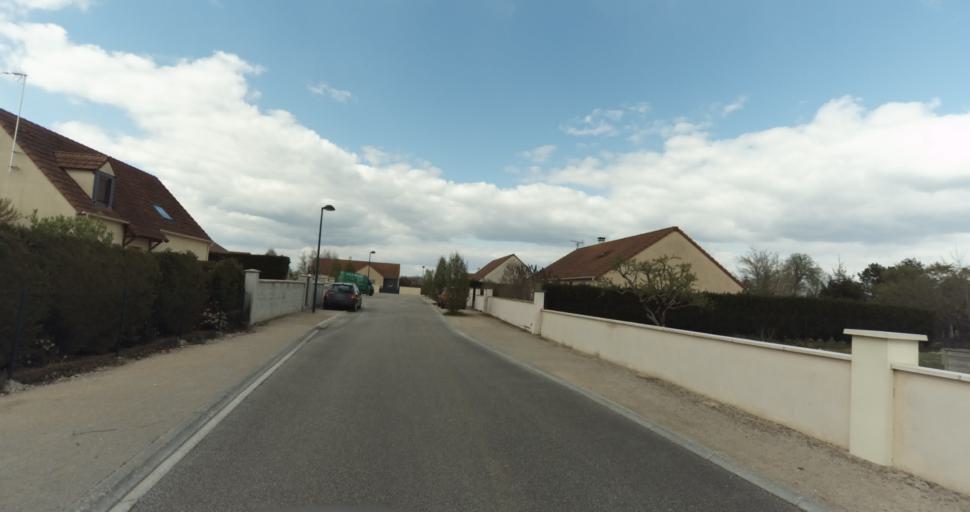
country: FR
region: Bourgogne
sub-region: Departement de la Cote-d'Or
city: Auxonne
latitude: 47.1963
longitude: 5.4089
